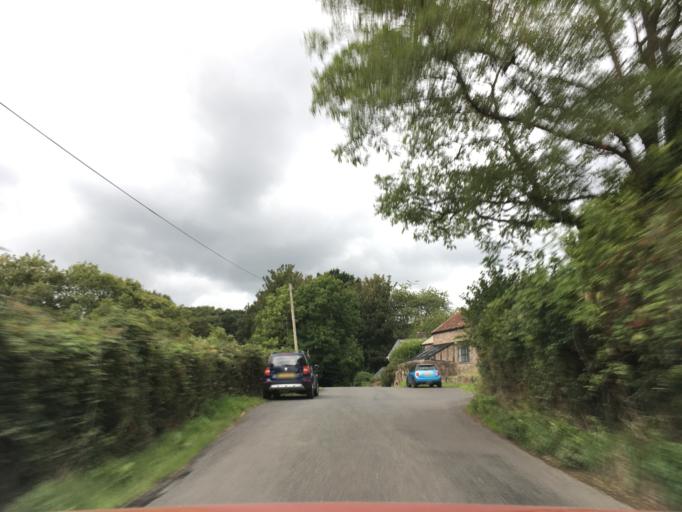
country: GB
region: Wales
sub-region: Newport
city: Llanvaches
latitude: 51.6318
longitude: -2.8163
